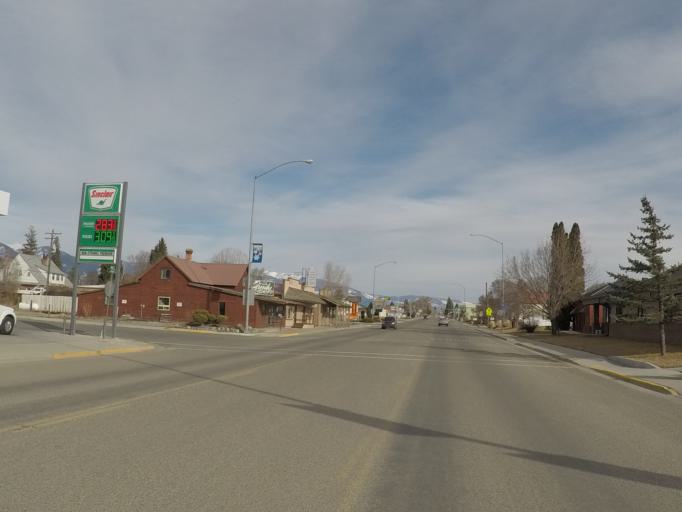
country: US
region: Idaho
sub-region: Lemhi County
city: Salmon
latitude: 45.1747
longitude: -113.8916
